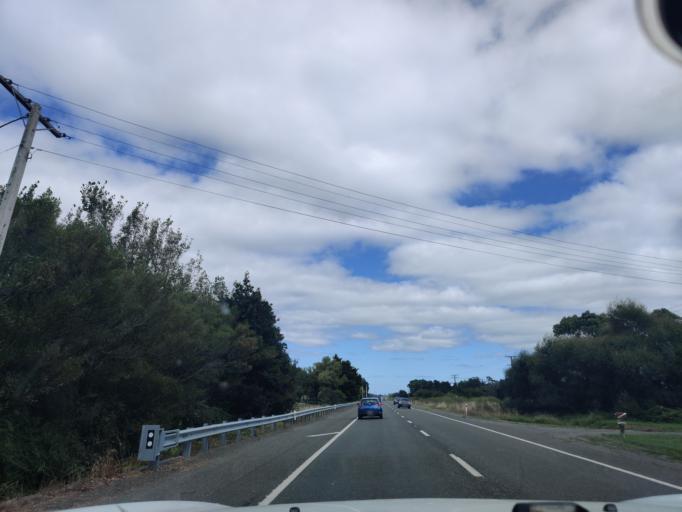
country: NZ
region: Manawatu-Wanganui
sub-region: Palmerston North City
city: Palmerston North
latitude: -40.3993
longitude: 175.5081
